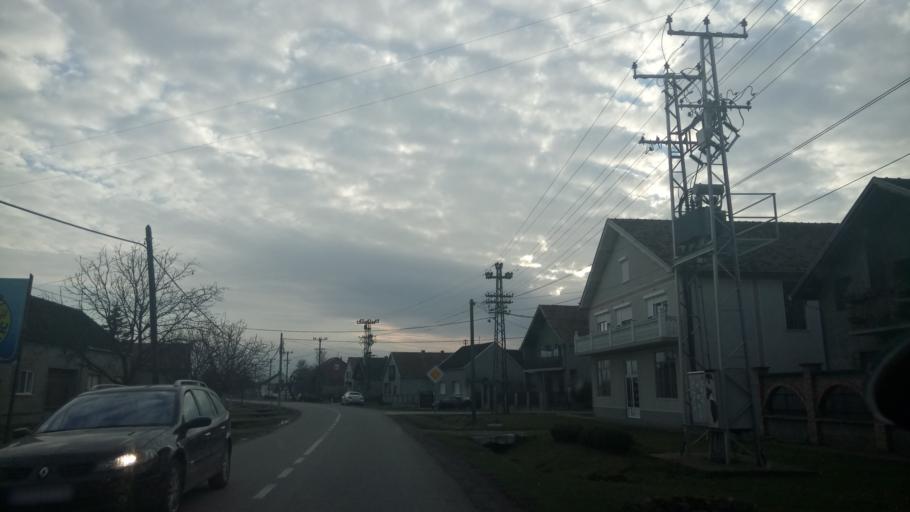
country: RS
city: Vojka
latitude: 44.9370
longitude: 20.1665
